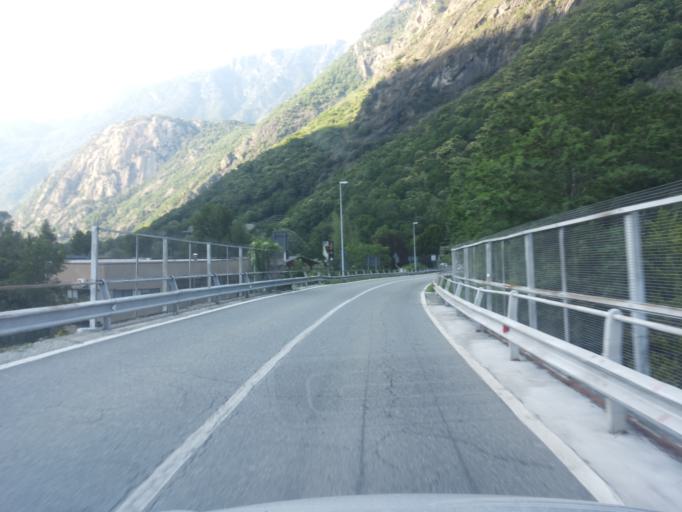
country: IT
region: Aosta Valley
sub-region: Valle d'Aosta
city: Hone
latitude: 45.6161
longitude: 7.7394
